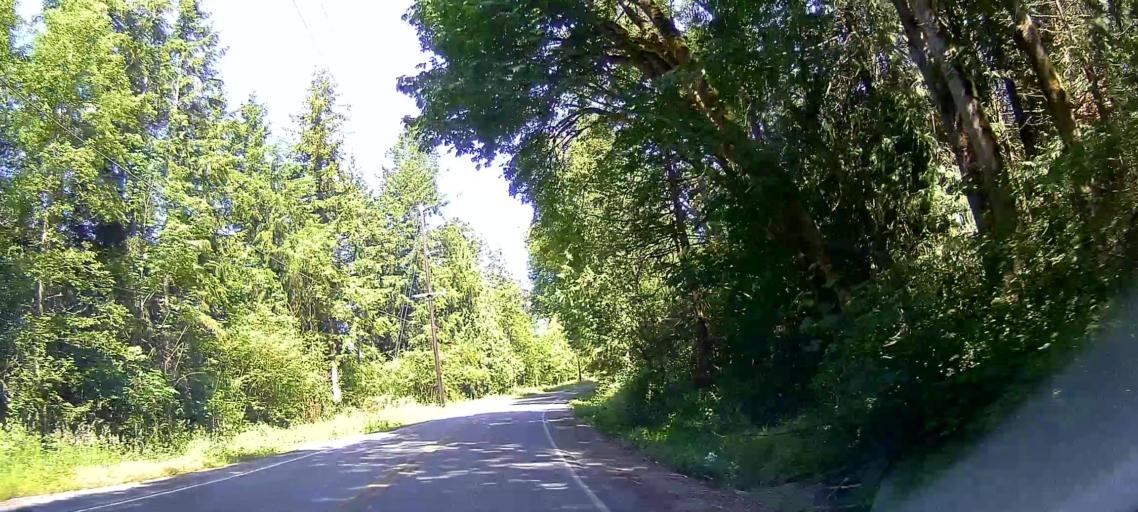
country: US
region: Washington
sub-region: Skagit County
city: Burlington
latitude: 48.5341
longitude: -122.3085
